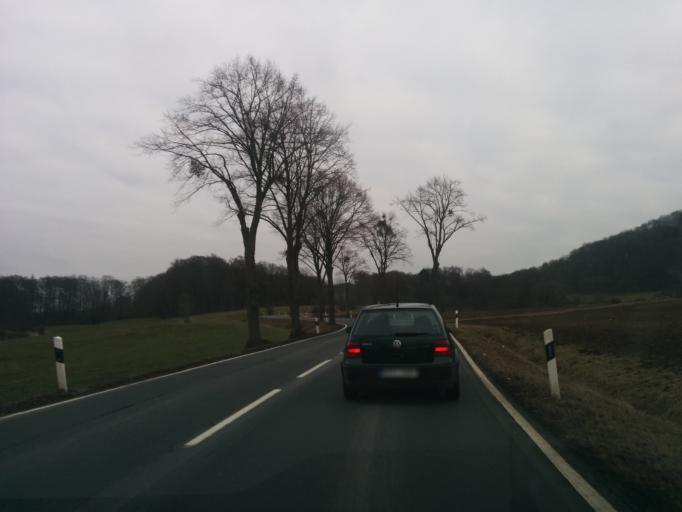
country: DE
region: Lower Saxony
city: Waake
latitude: 51.5984
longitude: 10.0313
